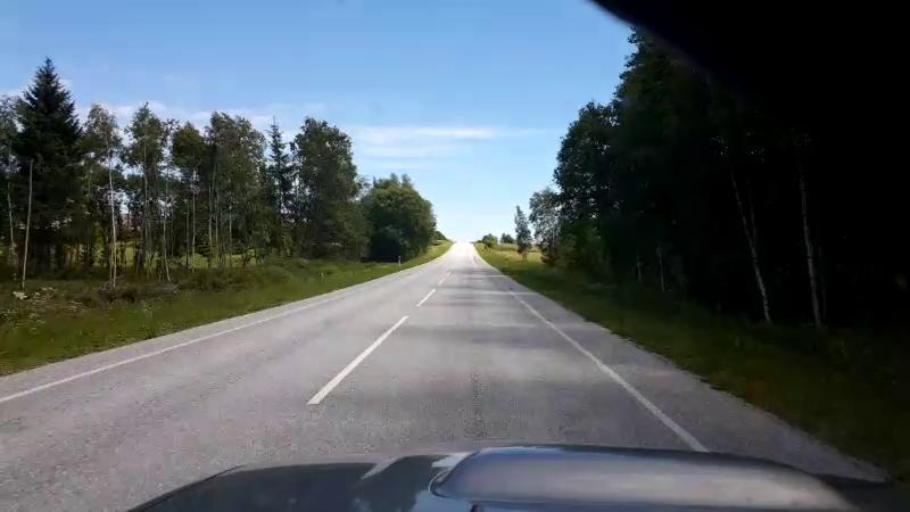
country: EE
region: Jaervamaa
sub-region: Koeru vald
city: Koeru
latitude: 58.9683
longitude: 26.1398
